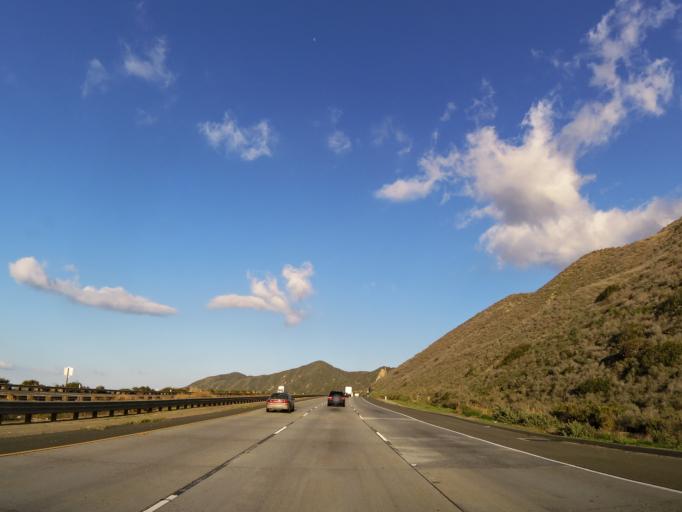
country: US
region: California
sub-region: Ventura County
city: Ventura
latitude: 34.3123
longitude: -119.3570
